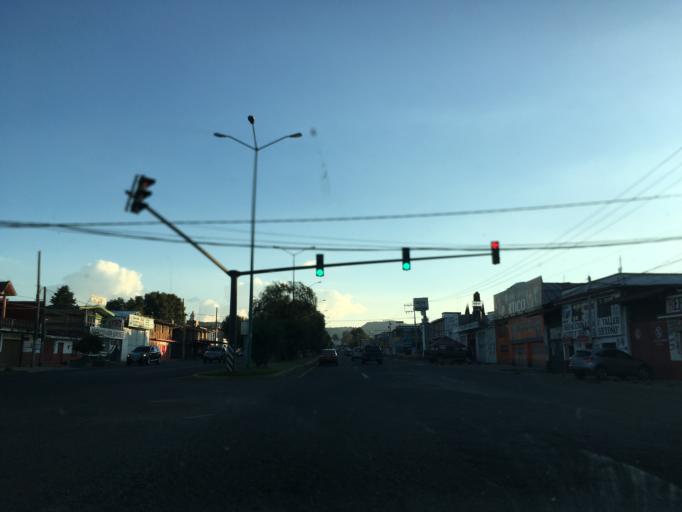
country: MX
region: Michoacan
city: Patzcuaro
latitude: 19.5163
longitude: -101.6178
